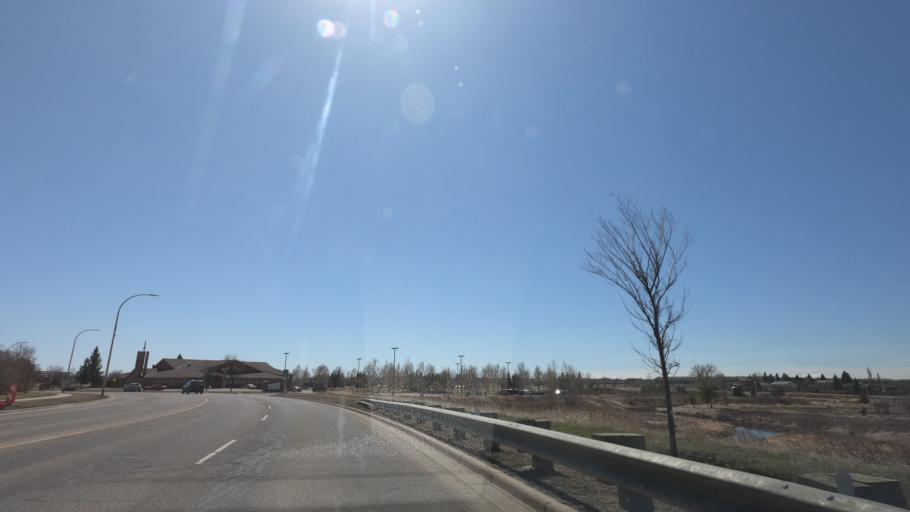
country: CA
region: Alberta
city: Airdrie
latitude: 51.2827
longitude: -114.0111
